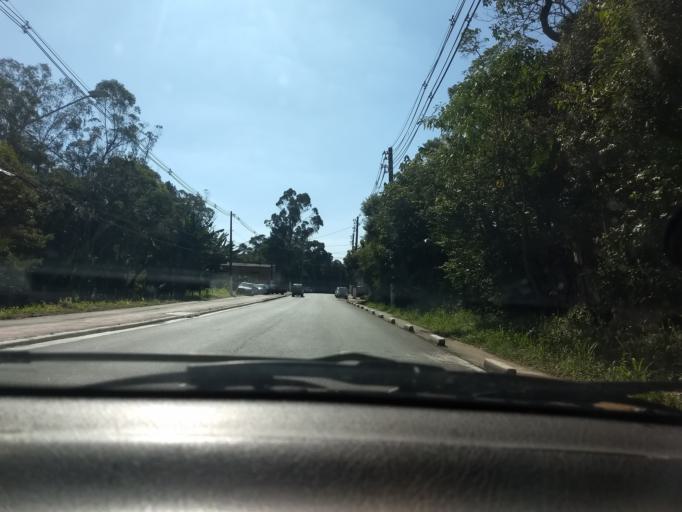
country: BR
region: Sao Paulo
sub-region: Embu-Guacu
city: Embu Guacu
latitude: -23.8323
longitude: -46.7309
